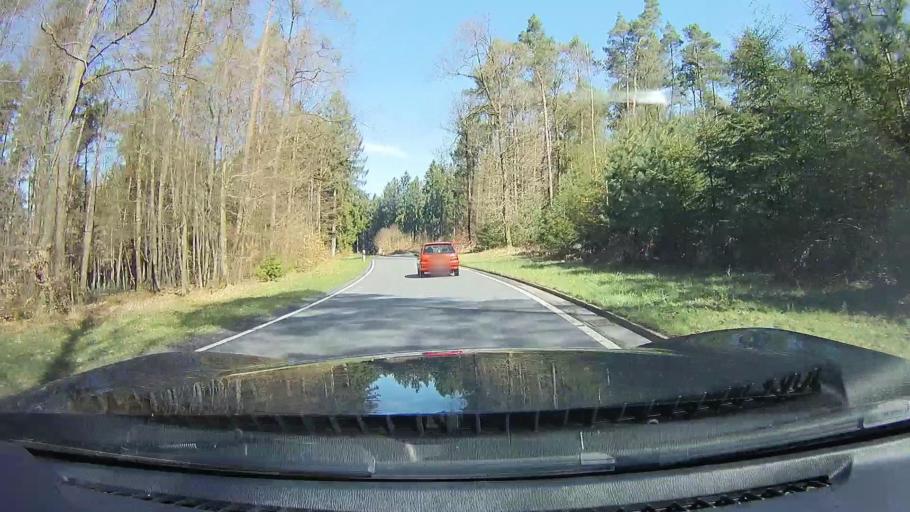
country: DE
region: Hesse
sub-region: Regierungsbezirk Darmstadt
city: Rothenberg
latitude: 49.5225
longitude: 8.9384
